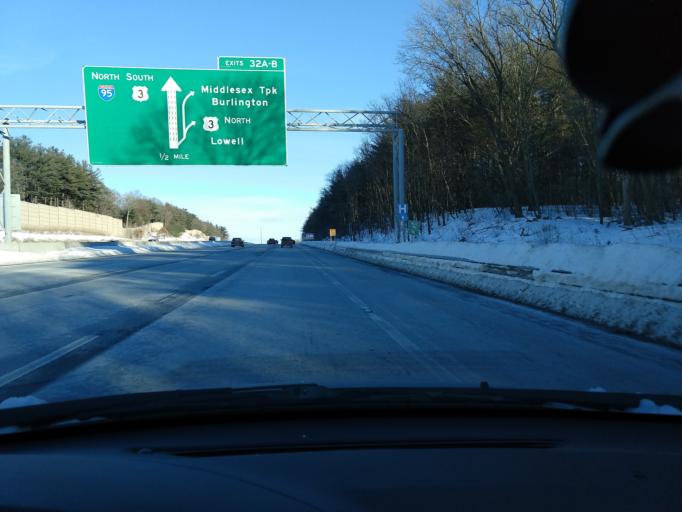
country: US
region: Massachusetts
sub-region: Middlesex County
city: Lexington
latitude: 42.4737
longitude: -71.2329
